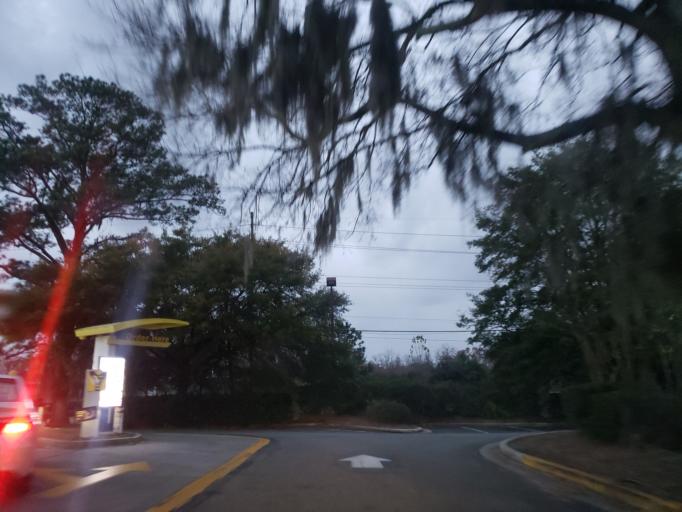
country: US
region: Georgia
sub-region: Chatham County
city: Thunderbolt
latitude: 32.0478
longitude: -81.0650
